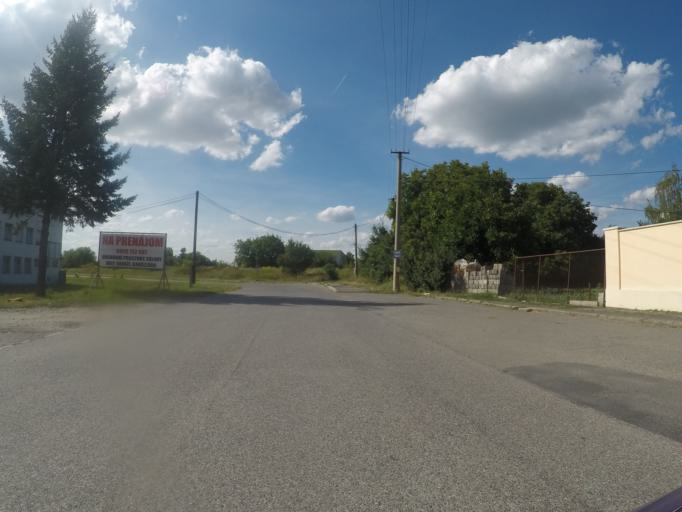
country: SK
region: Banskobystricky
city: Rimavska Sobota
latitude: 48.3893
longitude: 20.0138
